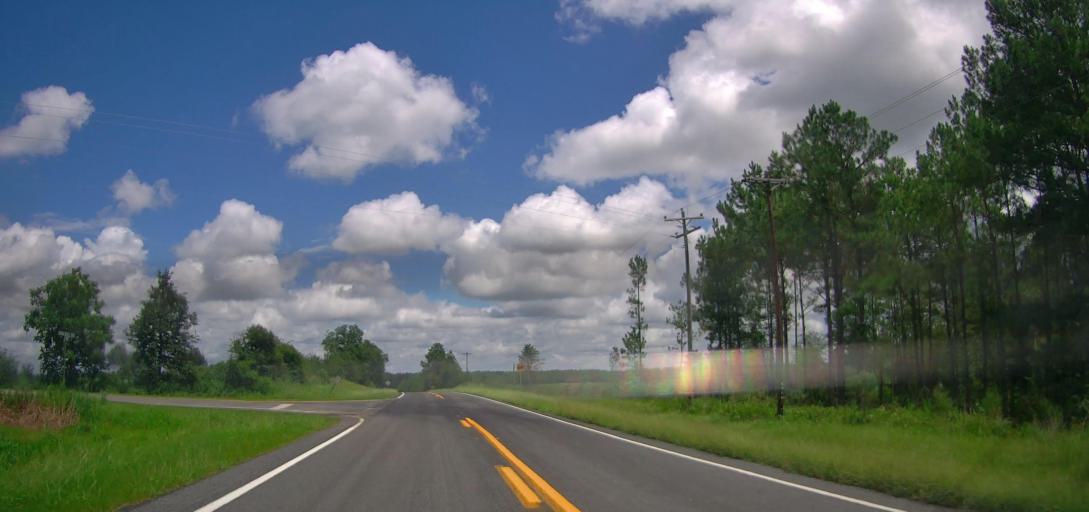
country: US
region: Georgia
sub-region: Turner County
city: Ashburn
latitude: 31.7797
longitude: -83.6084
